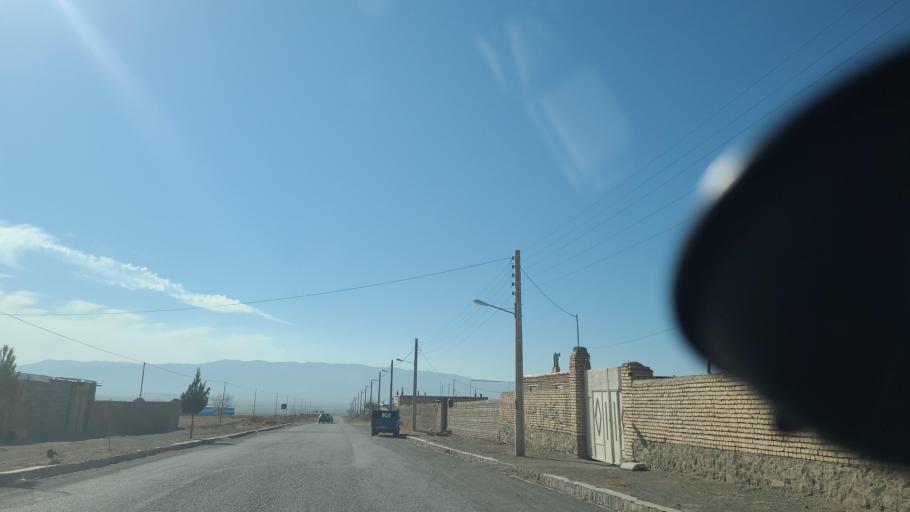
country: IR
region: Razavi Khorasan
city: Dowlatabad
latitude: 35.6191
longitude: 59.4765
